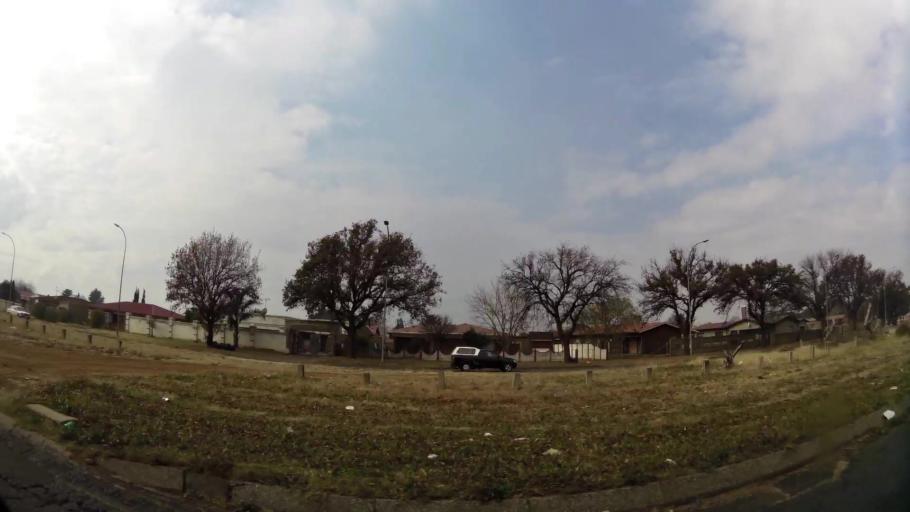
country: ZA
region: Gauteng
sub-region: Sedibeng District Municipality
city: Vanderbijlpark
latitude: -26.6801
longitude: 27.8351
